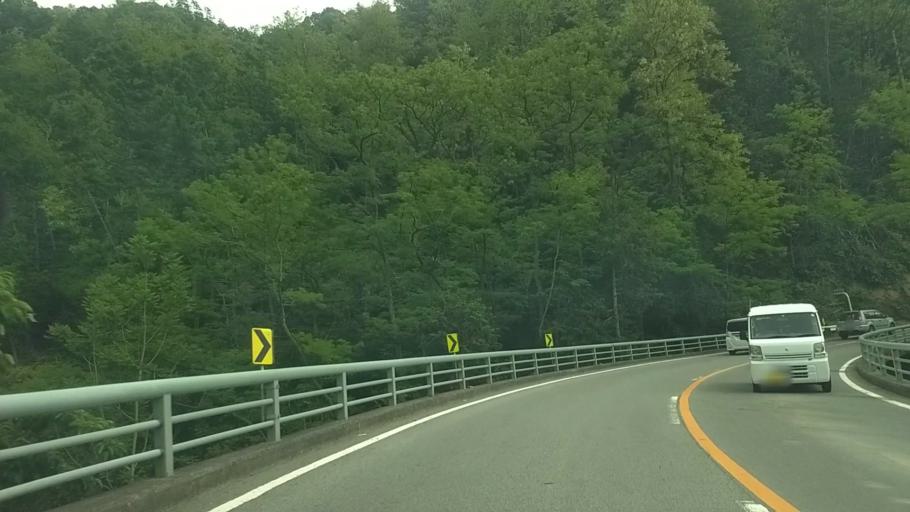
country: JP
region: Yamanashi
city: Isawa
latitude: 35.5643
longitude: 138.5945
